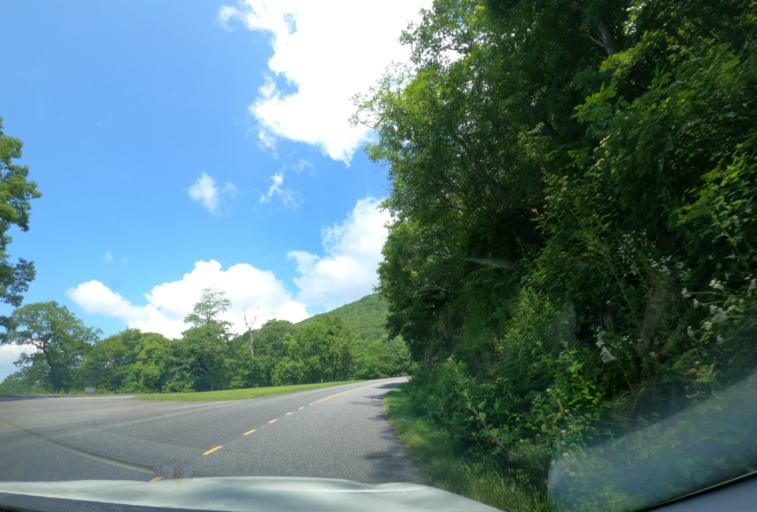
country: US
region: North Carolina
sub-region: Haywood County
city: Maggie Valley
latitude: 35.4526
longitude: -83.0925
